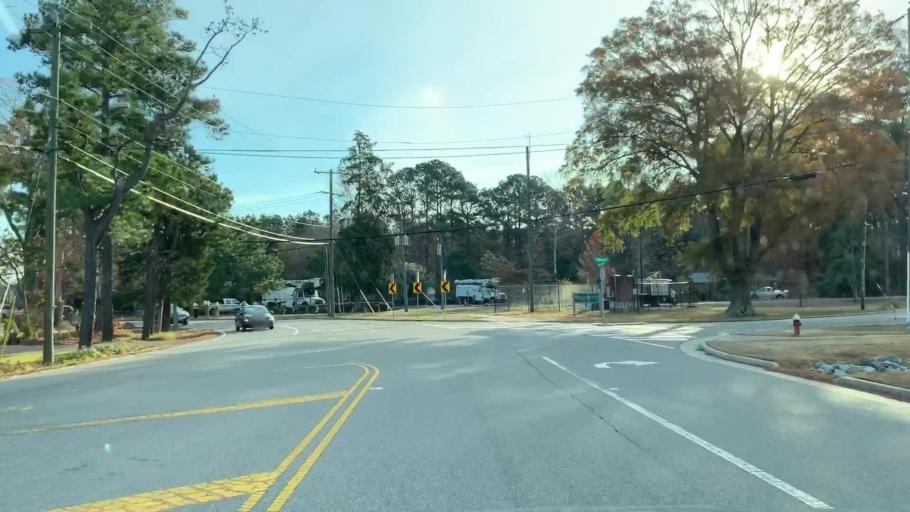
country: US
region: Virginia
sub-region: City of Chesapeake
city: Chesapeake
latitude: 36.7605
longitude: -76.1426
